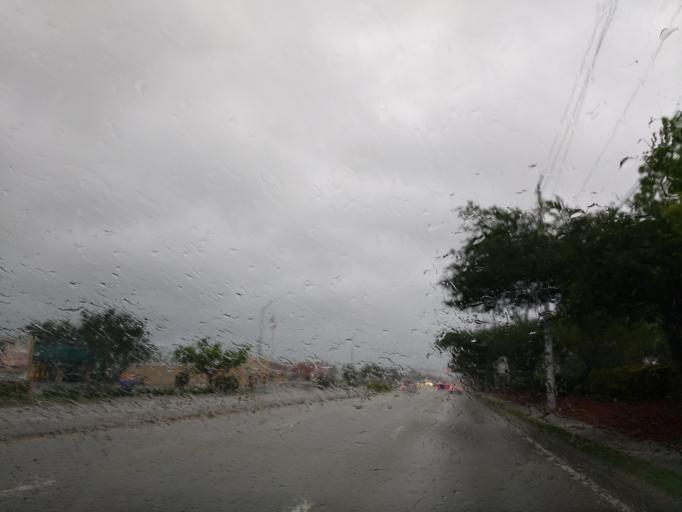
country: US
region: Florida
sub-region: Collier County
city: Naples
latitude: 26.1364
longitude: -81.7664
